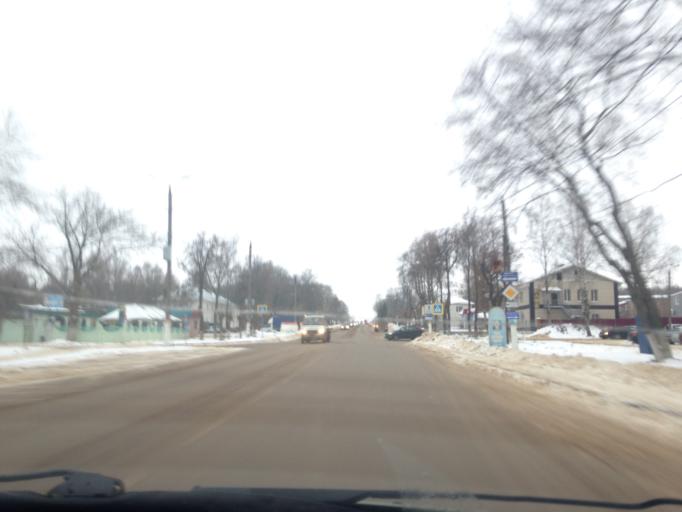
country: RU
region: Tula
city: Shchekino
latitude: 54.0054
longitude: 37.5121
